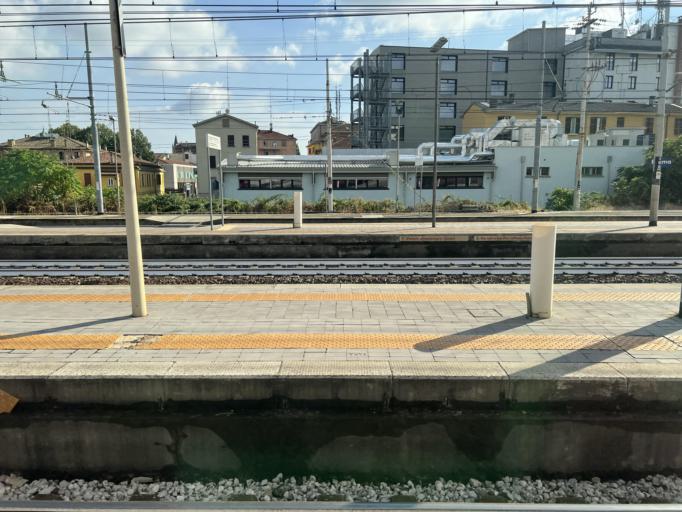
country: IT
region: Emilia-Romagna
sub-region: Provincia di Parma
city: Parma
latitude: 44.8098
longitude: 10.3311
